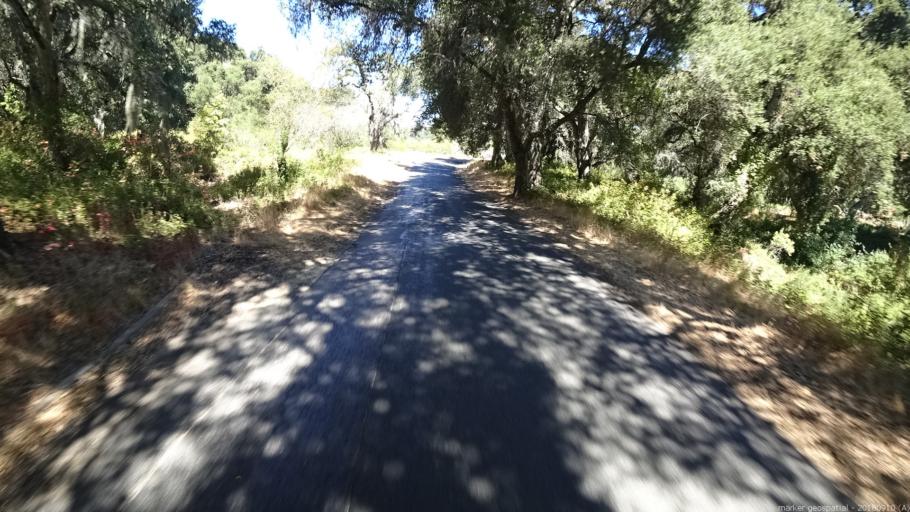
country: US
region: California
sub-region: Monterey County
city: Carmel Valley Village
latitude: 36.4420
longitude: -121.7972
